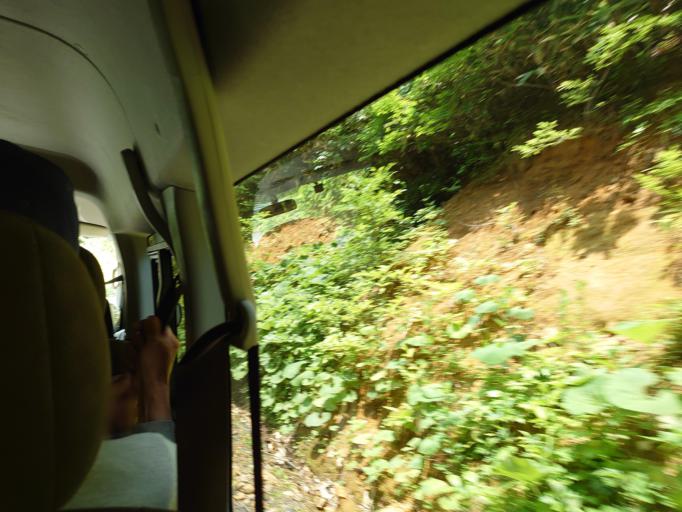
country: JP
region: Iwate
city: Ichinoseki
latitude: 38.9430
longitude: 140.8702
